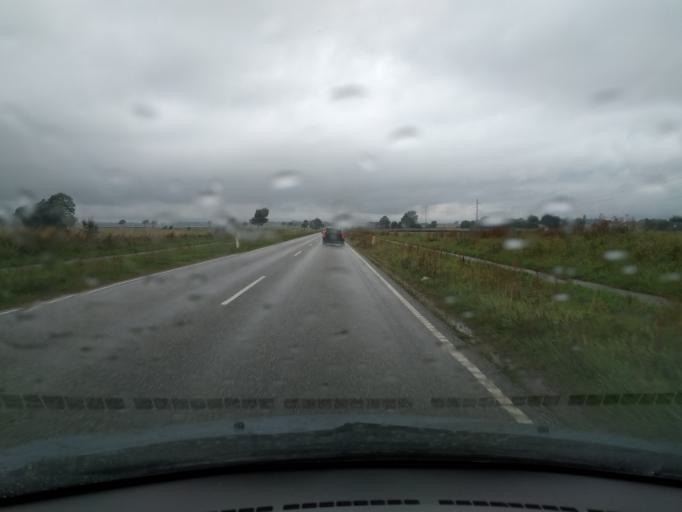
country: DK
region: Zealand
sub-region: Vordingborg Kommune
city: Neder Vindinge
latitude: 55.1236
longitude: 11.8191
